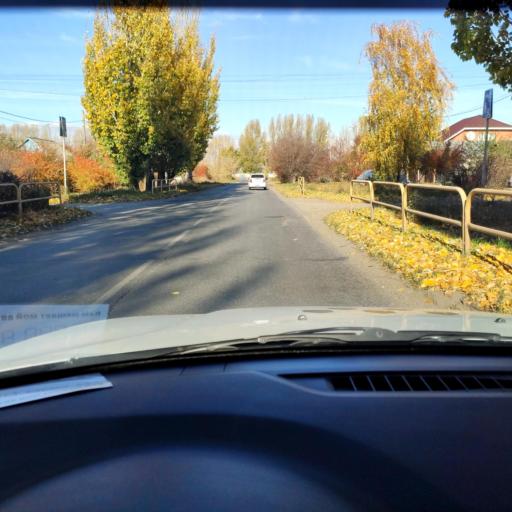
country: RU
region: Samara
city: Tol'yatti
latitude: 53.5387
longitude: 49.4164
